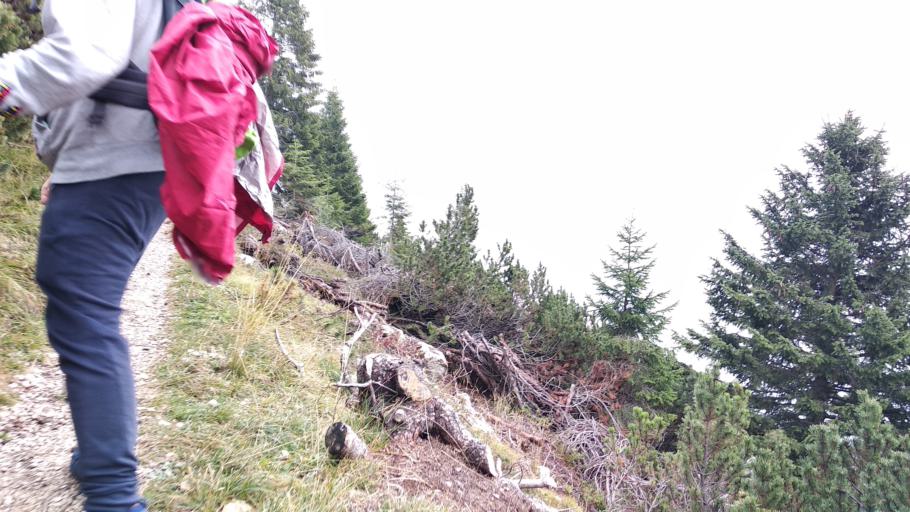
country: IT
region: Veneto
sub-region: Provincia di Vicenza
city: Roana
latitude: 45.9560
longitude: 11.4553
